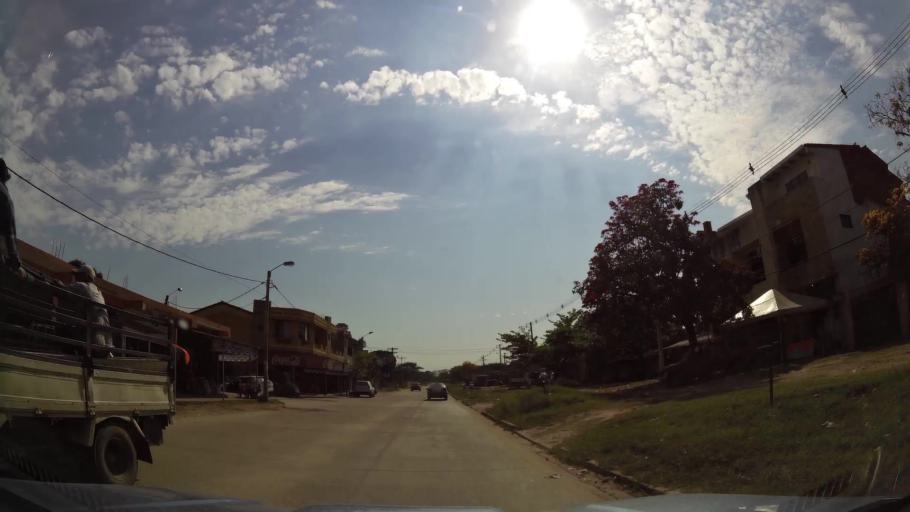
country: BO
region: Santa Cruz
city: Santa Cruz de la Sierra
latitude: -17.7240
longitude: -63.1550
